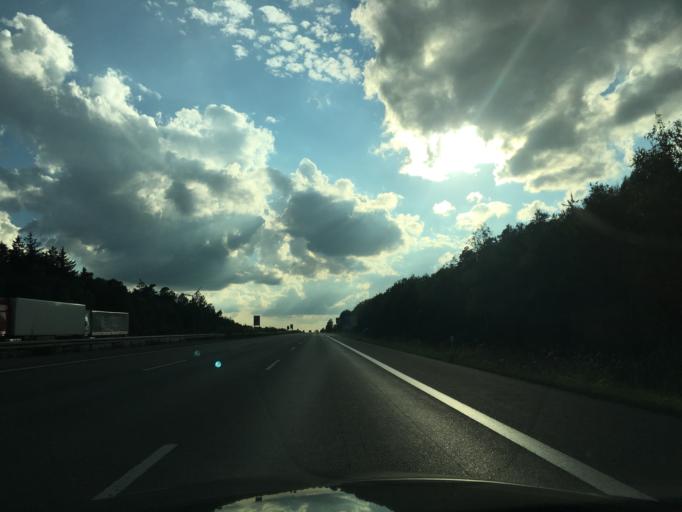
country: DE
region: Bavaria
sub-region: Regierungsbezirk Mittelfranken
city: Aurach
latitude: 49.2427
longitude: 10.3645
